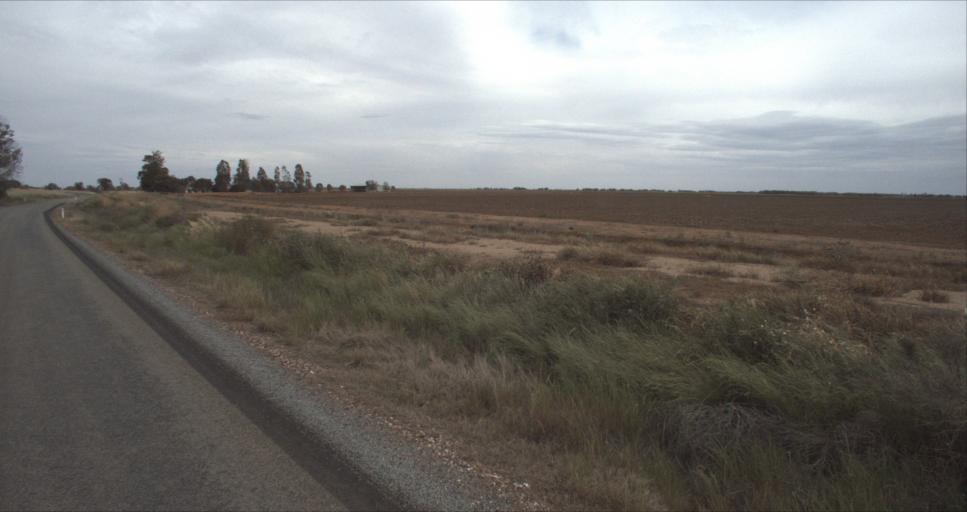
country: AU
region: New South Wales
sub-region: Leeton
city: Leeton
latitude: -34.4286
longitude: 146.3779
